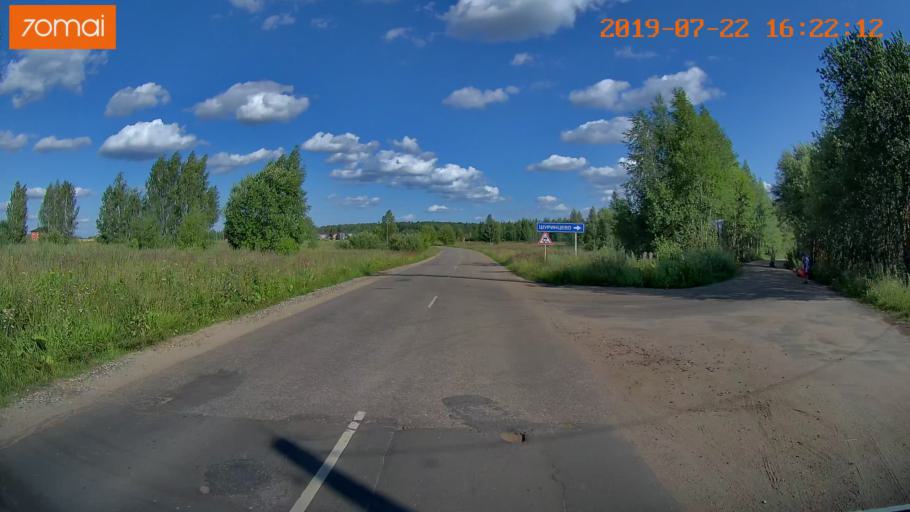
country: RU
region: Ivanovo
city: Novo-Talitsy
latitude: 57.0589
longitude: 40.8796
